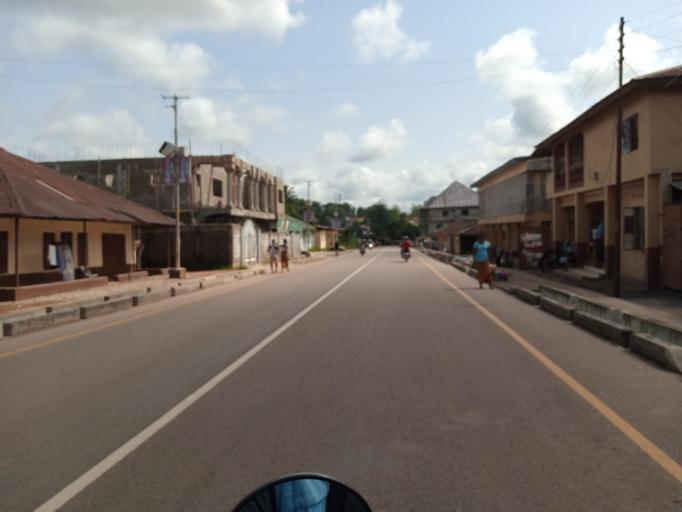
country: SL
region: Southern Province
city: Bo
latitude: 7.9713
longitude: -11.7382
